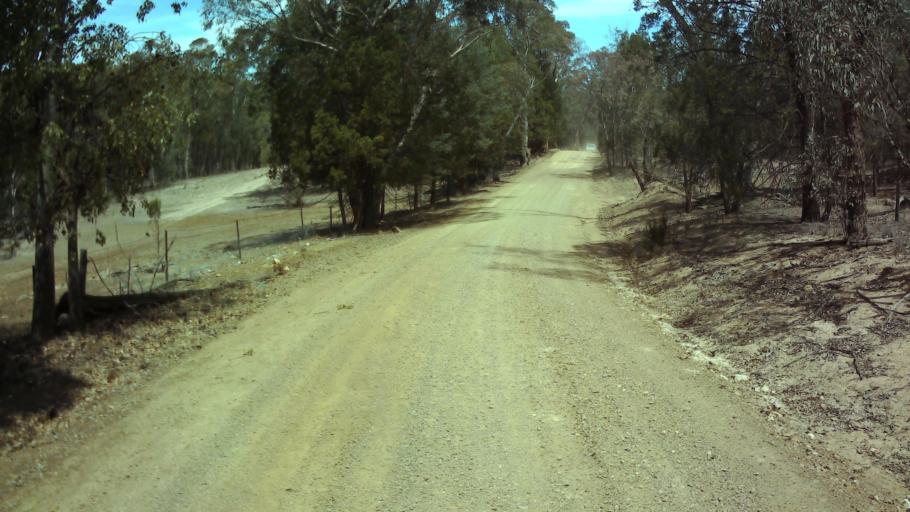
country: AU
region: New South Wales
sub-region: Weddin
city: Grenfell
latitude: -33.8173
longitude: 148.1658
